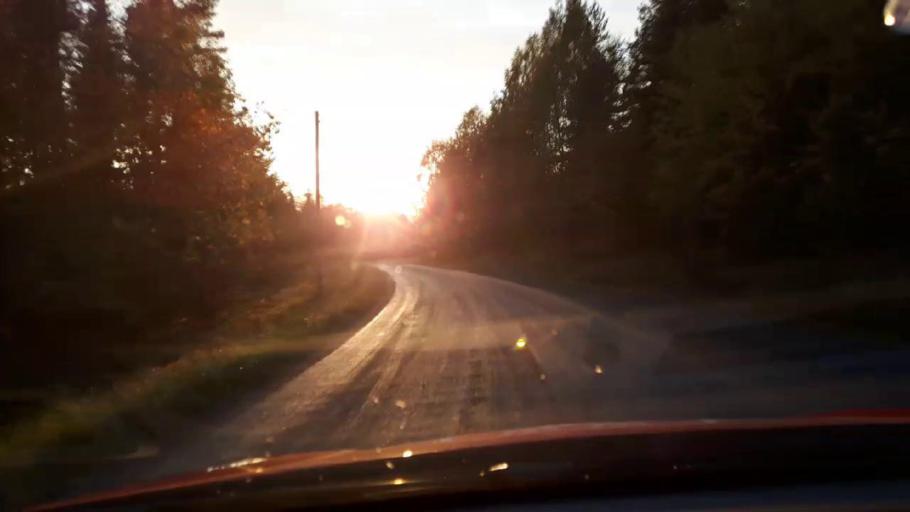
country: SE
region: Jaemtland
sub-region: OEstersunds Kommun
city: Lit
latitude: 63.2843
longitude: 14.7408
